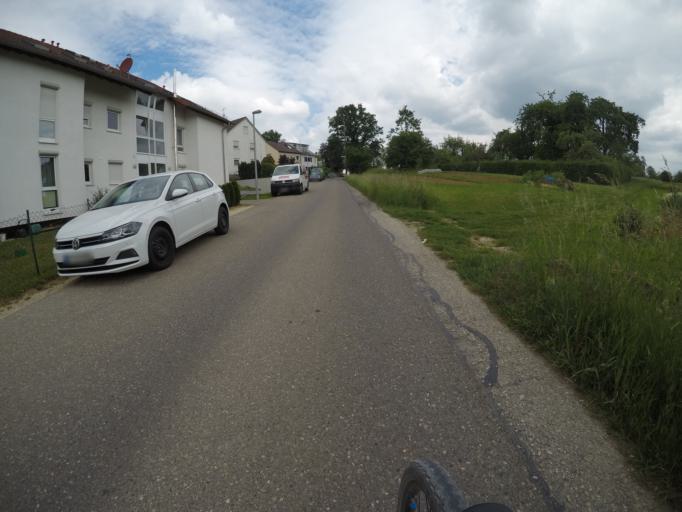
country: DE
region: Baden-Wuerttemberg
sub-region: Regierungsbezirk Stuttgart
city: Kongen
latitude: 48.6889
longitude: 9.3718
